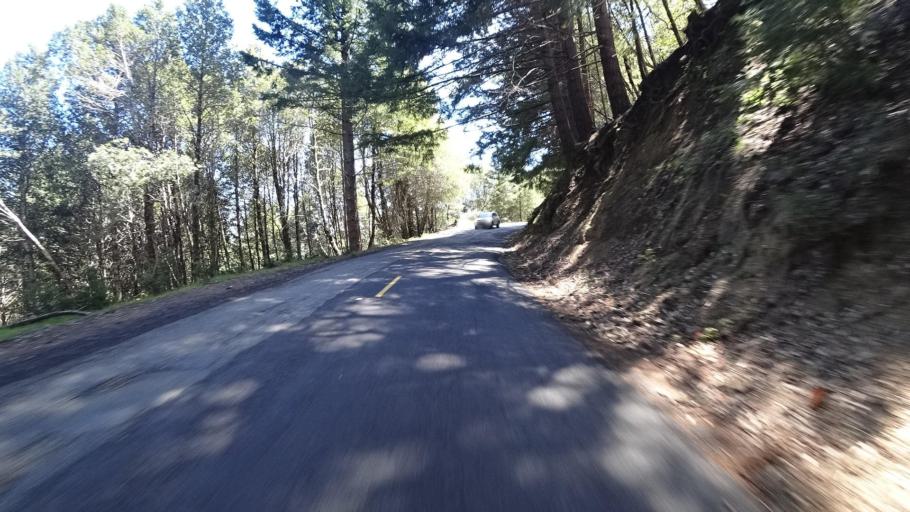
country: US
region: California
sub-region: Humboldt County
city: Rio Dell
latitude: 40.2984
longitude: -124.0566
